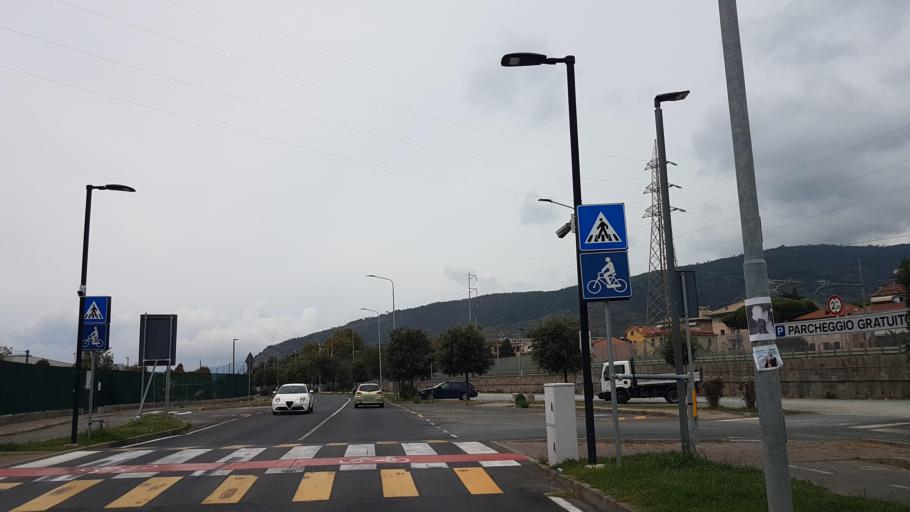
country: IT
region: Liguria
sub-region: Provincia di Genova
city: Sestri Levante
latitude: 44.2710
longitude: 9.4085
